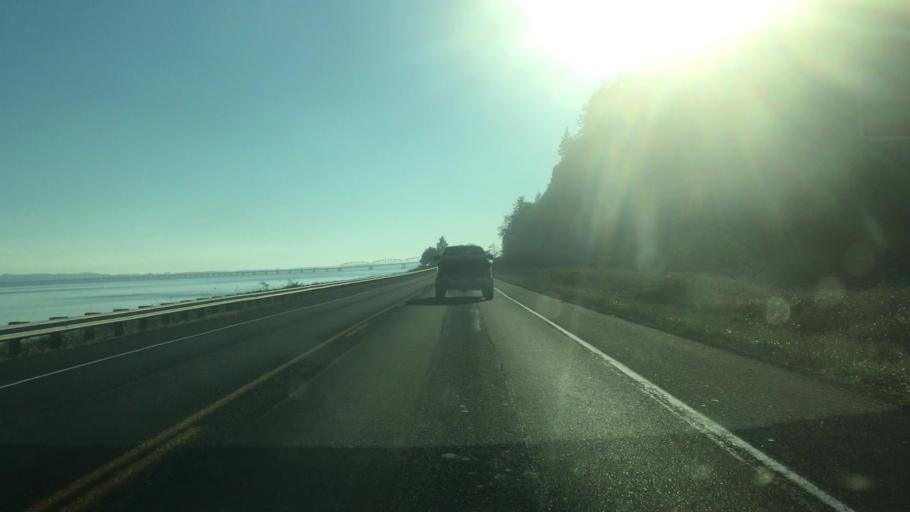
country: US
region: Oregon
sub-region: Clatsop County
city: Astoria
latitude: 46.2533
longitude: -123.8551
